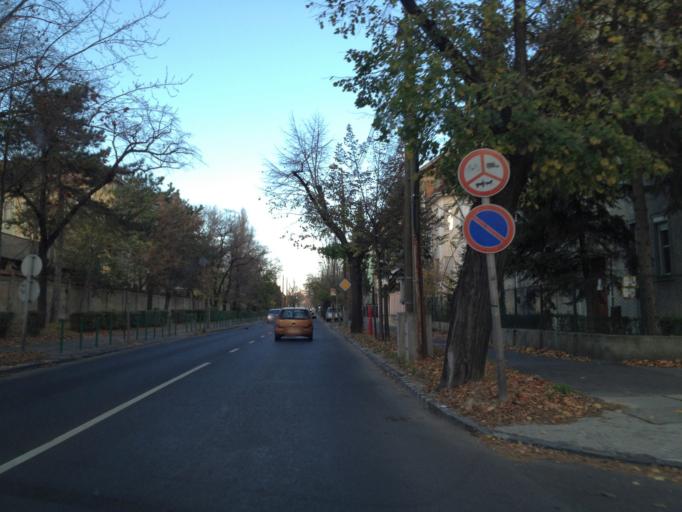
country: HU
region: Gyor-Moson-Sopron
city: Gyor
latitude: 47.6764
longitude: 17.6399
